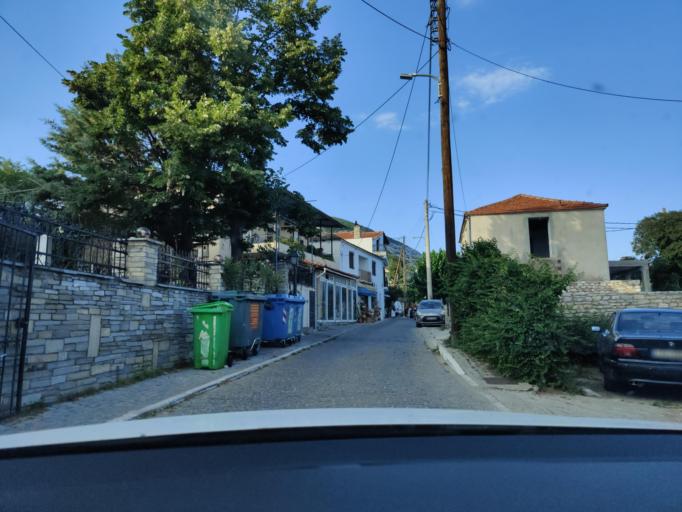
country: GR
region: East Macedonia and Thrace
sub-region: Nomos Kavalas
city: Potamia
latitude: 40.6590
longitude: 24.6917
